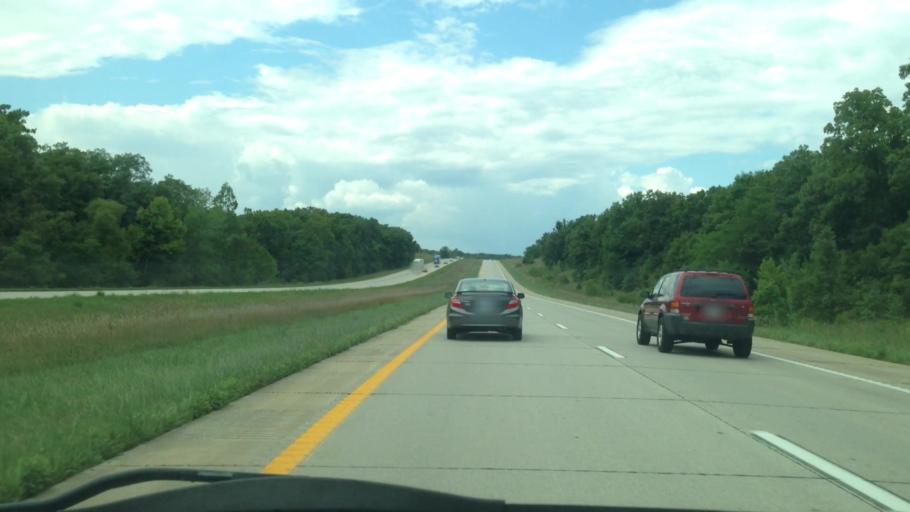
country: US
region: Missouri
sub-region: Pike County
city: Bowling Green
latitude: 39.3893
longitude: -91.2311
